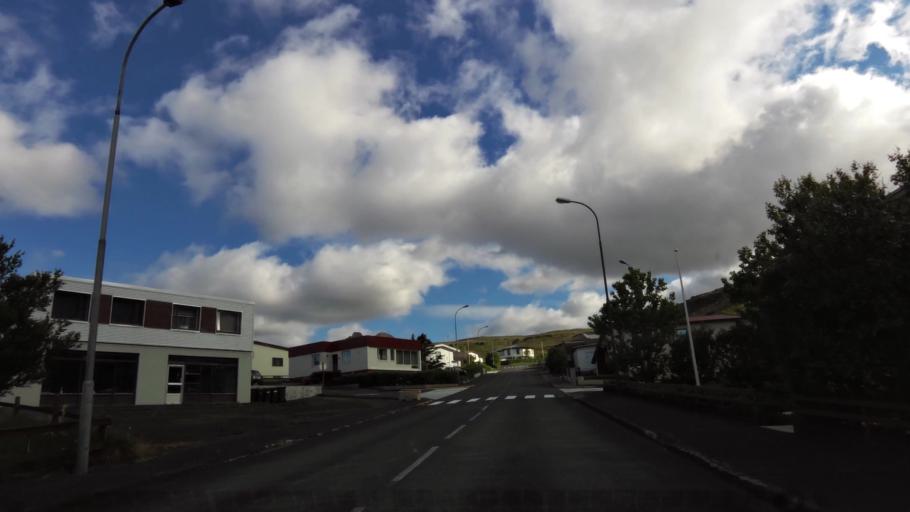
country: IS
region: West
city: Olafsvik
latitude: 64.8926
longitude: -23.7098
